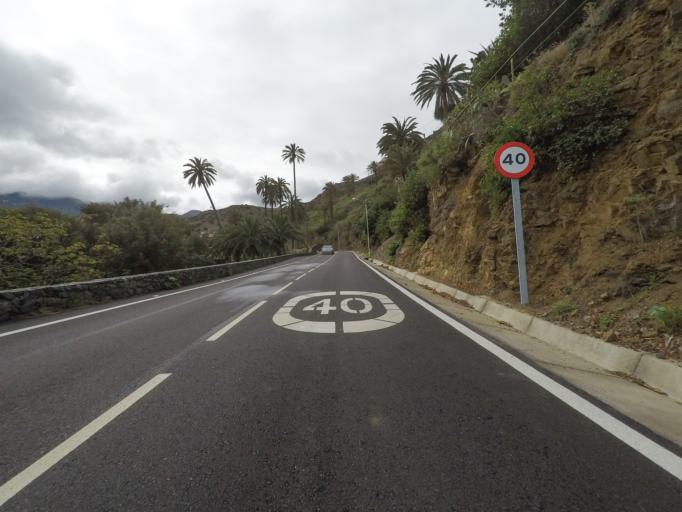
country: ES
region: Canary Islands
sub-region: Provincia de Santa Cruz de Tenerife
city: Vallehermosa
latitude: 28.1880
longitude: -17.2631
